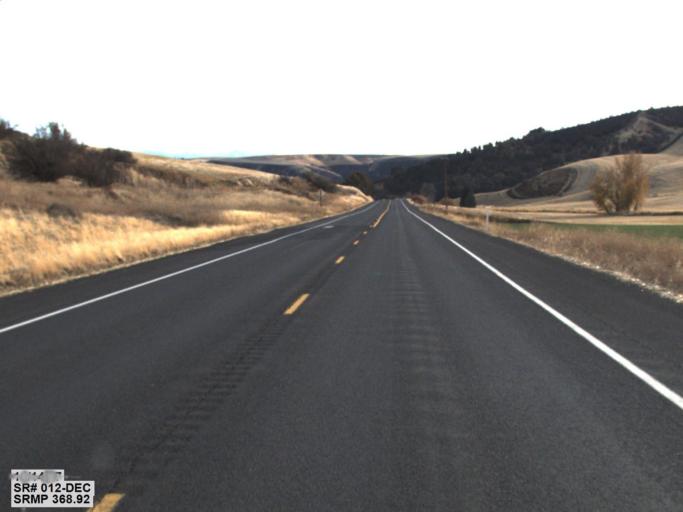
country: US
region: Washington
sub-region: Columbia County
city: Dayton
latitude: 46.3415
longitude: -117.9793
